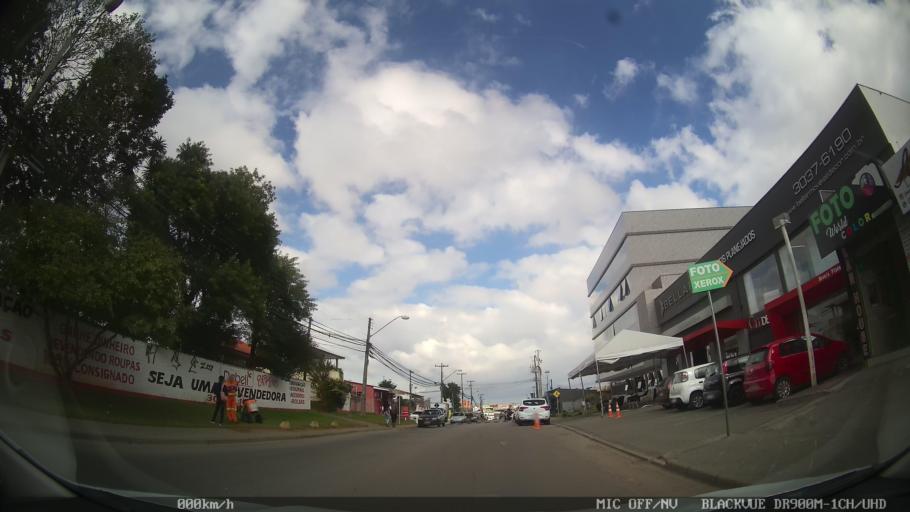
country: BR
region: Parana
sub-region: Colombo
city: Colombo
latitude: -25.3616
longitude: -49.1859
